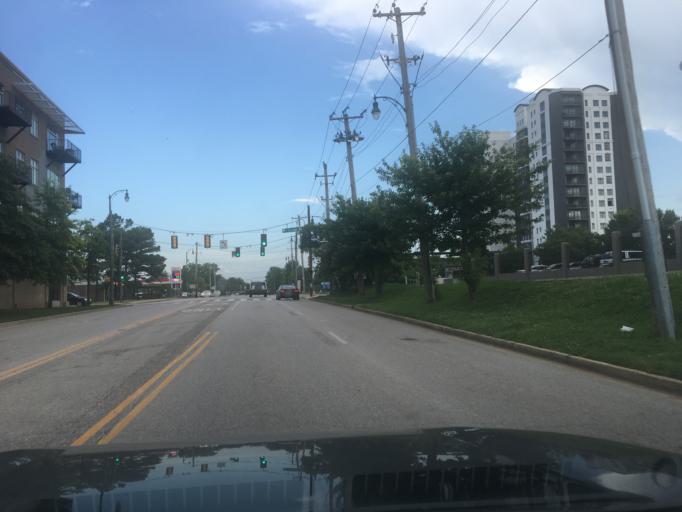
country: US
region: Tennessee
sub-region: Shelby County
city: Memphis
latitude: 35.1303
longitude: -90.0668
